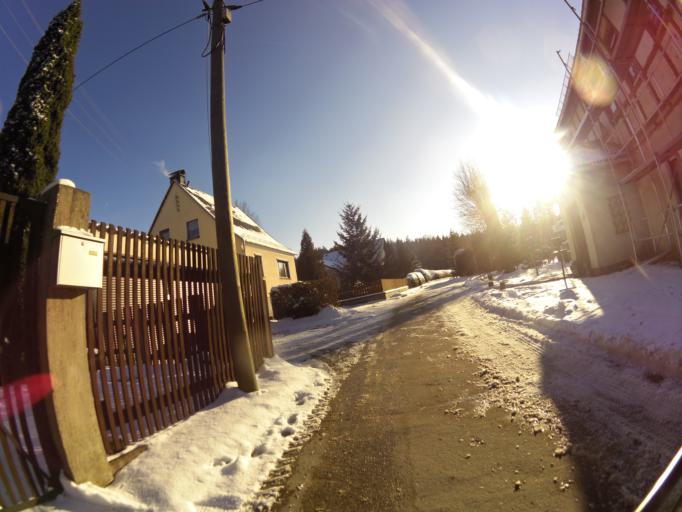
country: DE
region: Thuringia
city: Tanna
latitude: 50.4871
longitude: 11.8783
